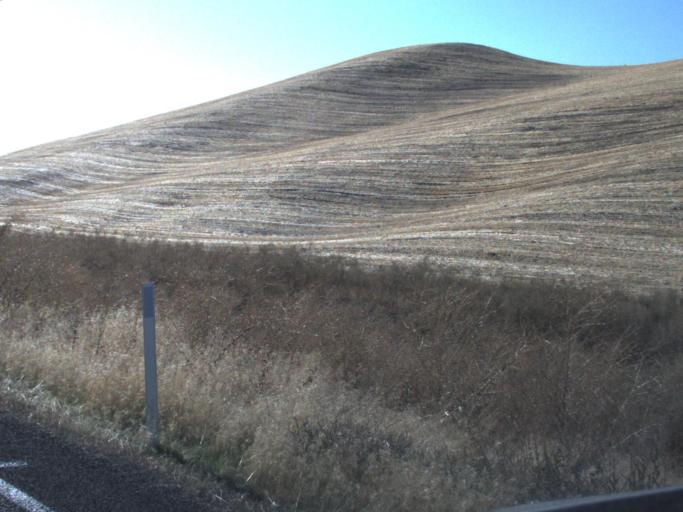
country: US
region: Washington
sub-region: Walla Walla County
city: Walla Walla
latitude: 46.2392
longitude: -118.3684
